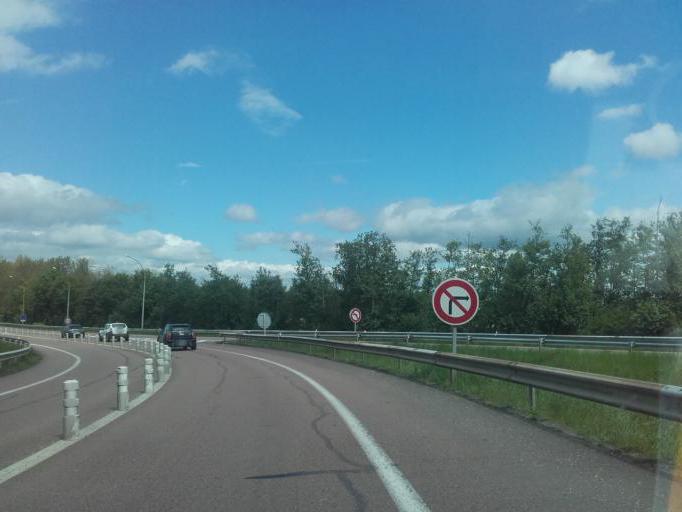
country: FR
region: Bourgogne
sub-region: Departement de Saone-et-Loire
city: Saint-Remy
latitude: 46.7515
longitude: 4.8329
